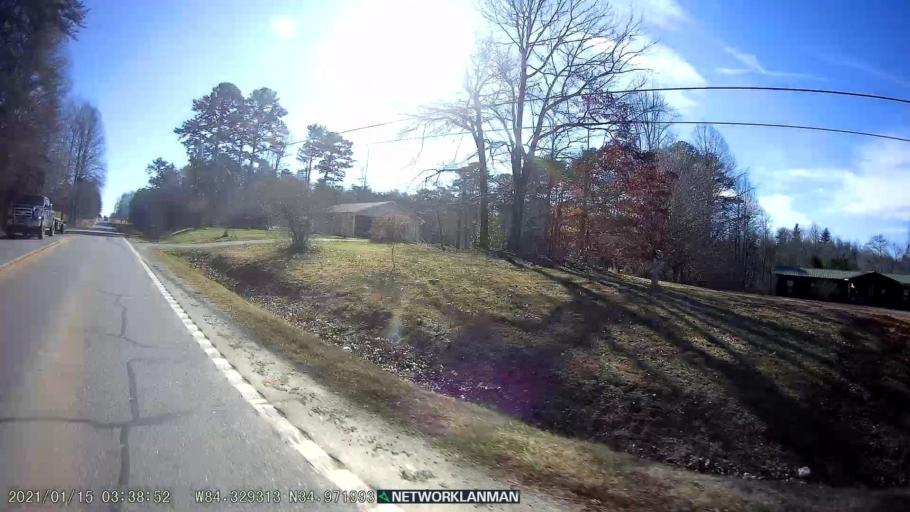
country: US
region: Georgia
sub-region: Fannin County
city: McCaysville
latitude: 34.9716
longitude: -84.3292
